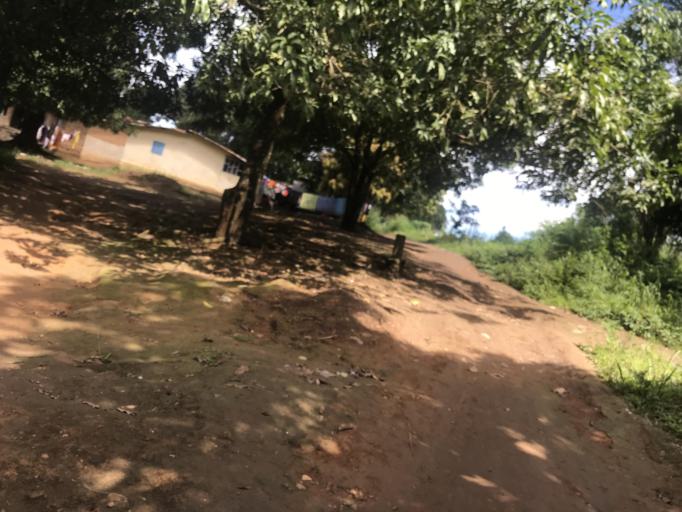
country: SL
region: Eastern Province
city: Koidu
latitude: 8.6461
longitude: -10.9871
